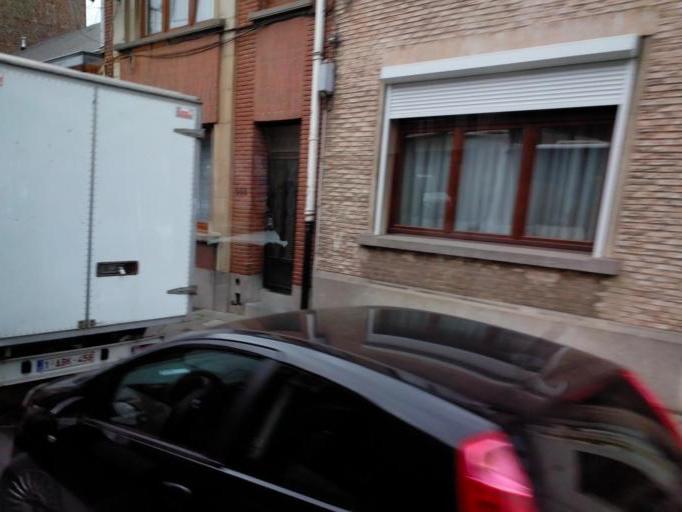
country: BE
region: Flanders
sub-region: Provincie Vlaams-Brabant
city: Diegem
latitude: 50.8573
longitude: 4.4066
